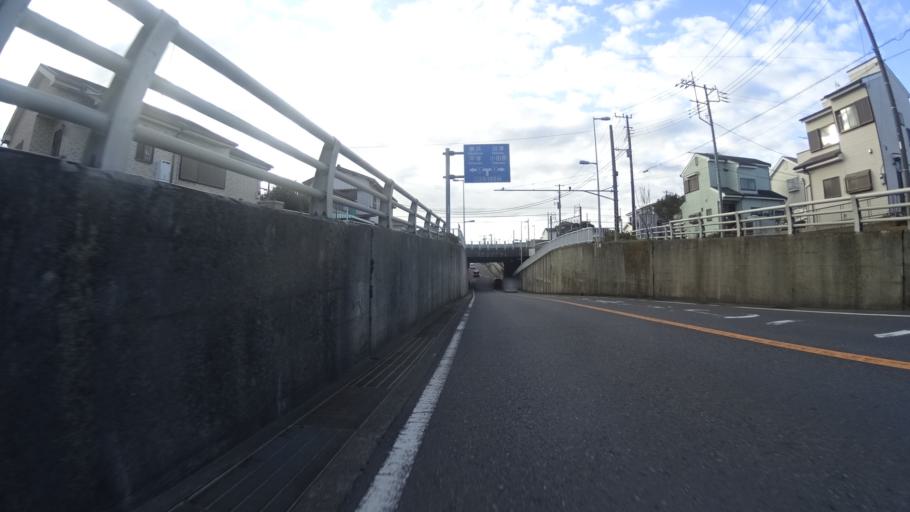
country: JP
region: Kanagawa
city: Ninomiya
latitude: 35.3064
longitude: 139.2775
